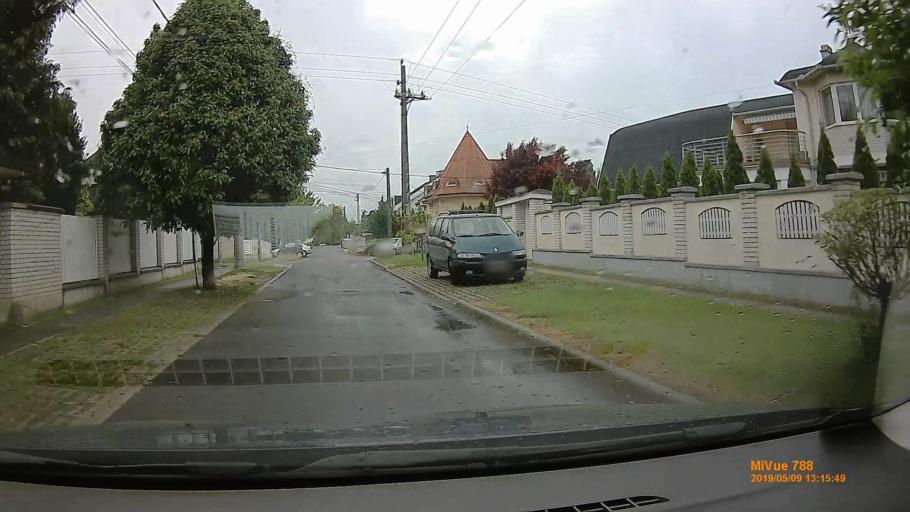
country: HU
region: Budapest
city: Budapest XVI. keruelet
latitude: 47.5411
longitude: 19.1815
